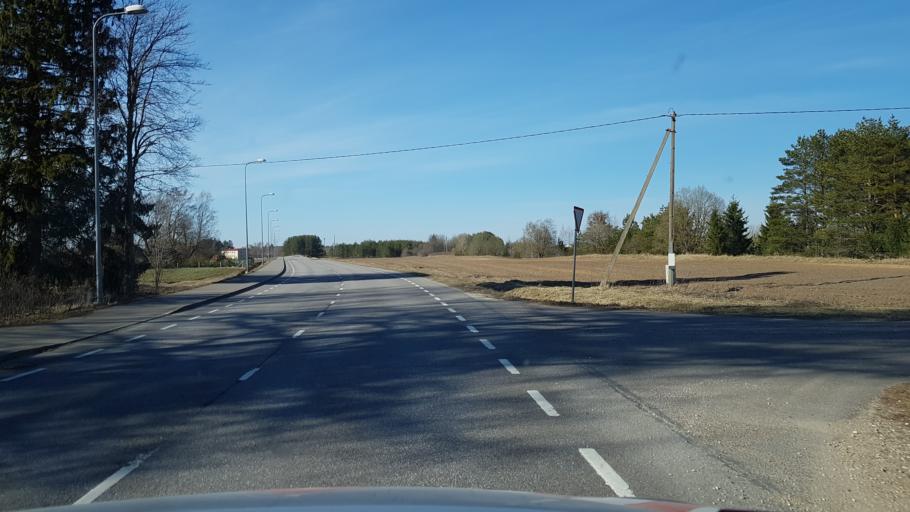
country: EE
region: Laeaene-Virumaa
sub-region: Vinni vald
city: Vinni
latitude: 59.1499
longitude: 26.5935
